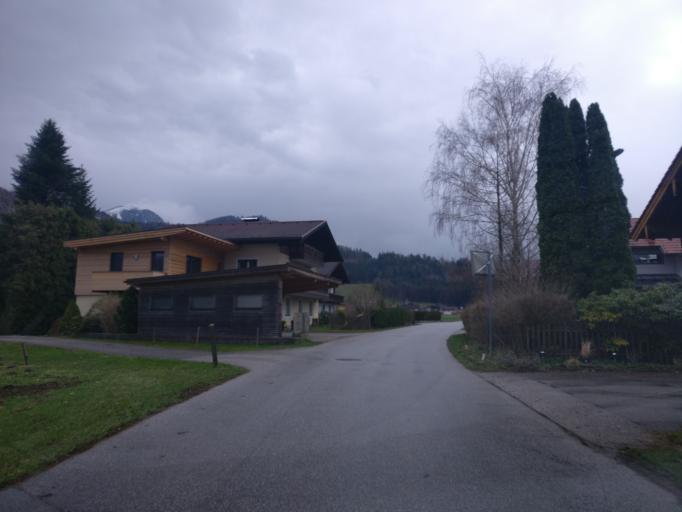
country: AT
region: Salzburg
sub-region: Politischer Bezirk Hallein
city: Kuchl
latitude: 47.6291
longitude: 13.1687
